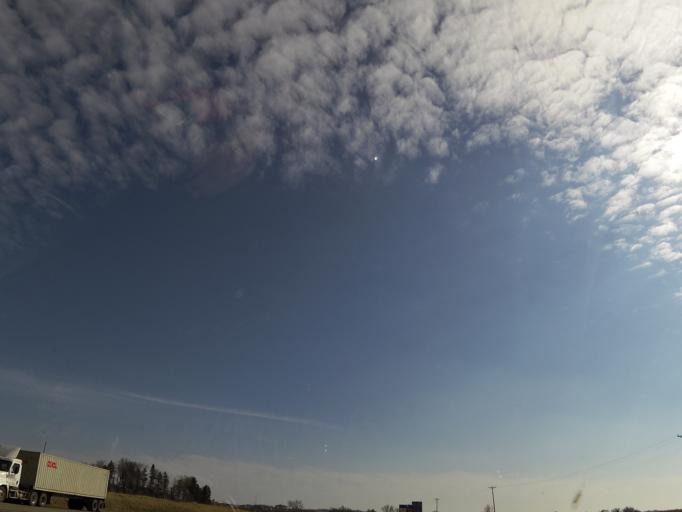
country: US
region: Minnesota
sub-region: Steele County
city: Medford
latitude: 44.1532
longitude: -93.2575
